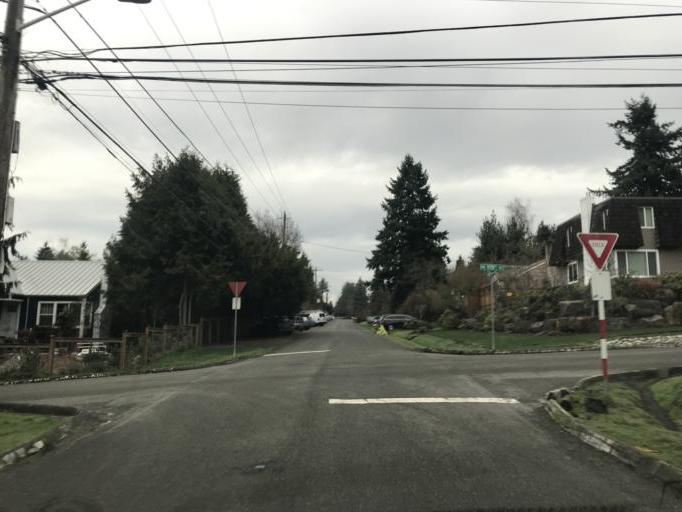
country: US
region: Washington
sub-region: King County
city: Lake Forest Park
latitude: 47.7117
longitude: -122.2853
